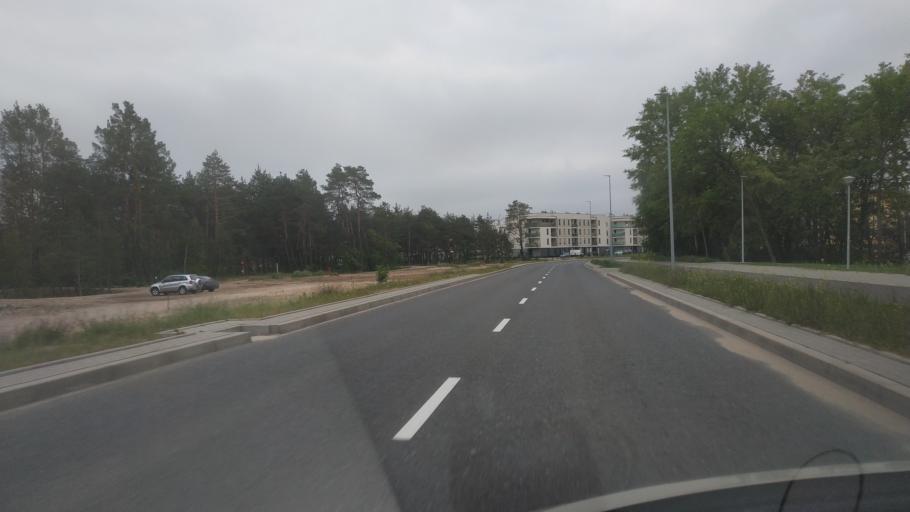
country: PL
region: Kujawsko-Pomorskie
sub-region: Torun
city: Torun
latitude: 53.0497
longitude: 18.6042
